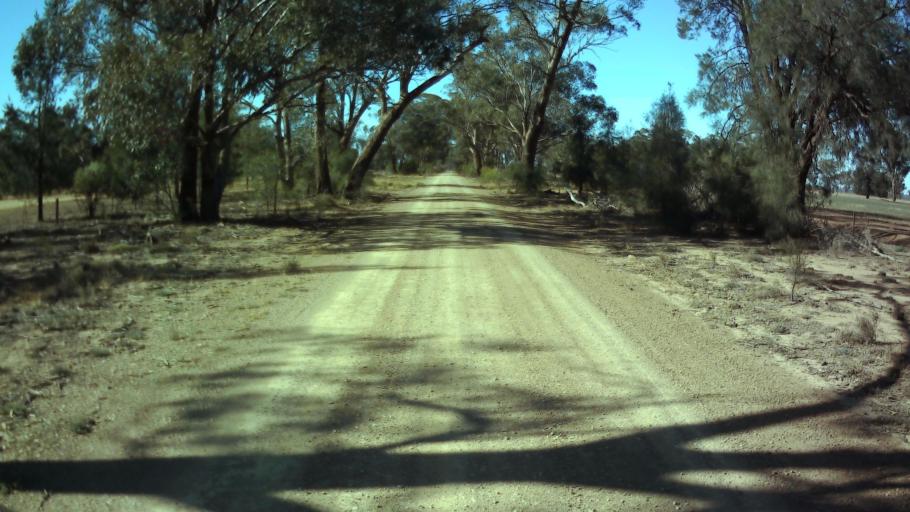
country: AU
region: New South Wales
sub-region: Weddin
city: Grenfell
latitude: -33.9360
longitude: 147.8719
